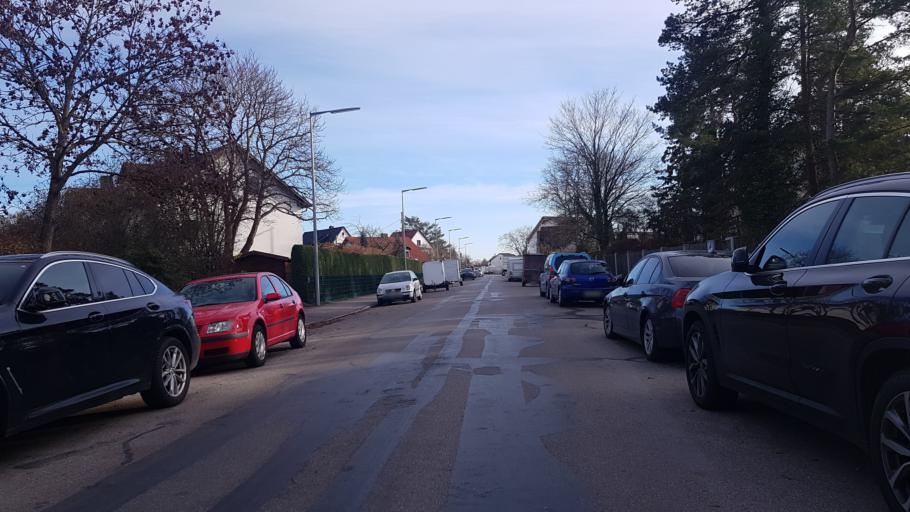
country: DE
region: Bavaria
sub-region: Upper Bavaria
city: Oberschleissheim
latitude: 48.2135
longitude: 11.5356
